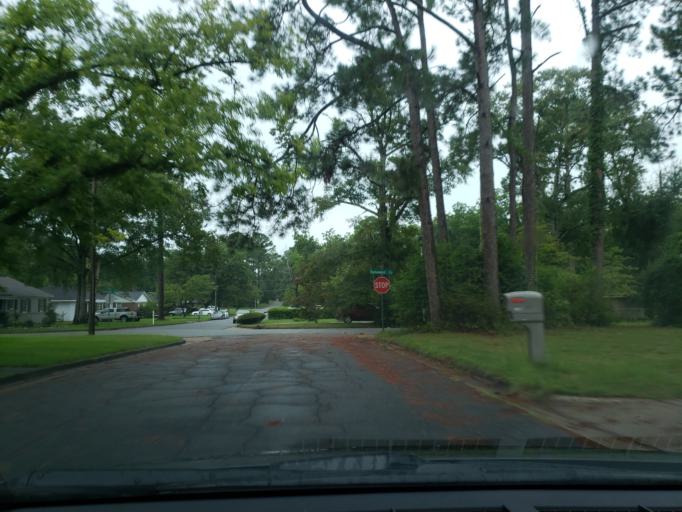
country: US
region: Georgia
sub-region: Dougherty County
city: Albany
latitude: 31.6062
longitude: -84.1865
